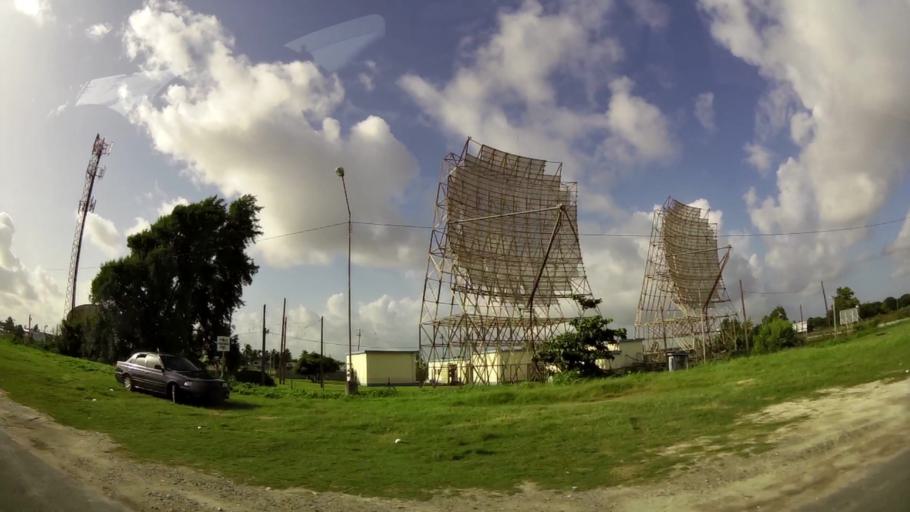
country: GY
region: Demerara-Mahaica
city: Georgetown
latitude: 6.8253
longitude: -58.1472
